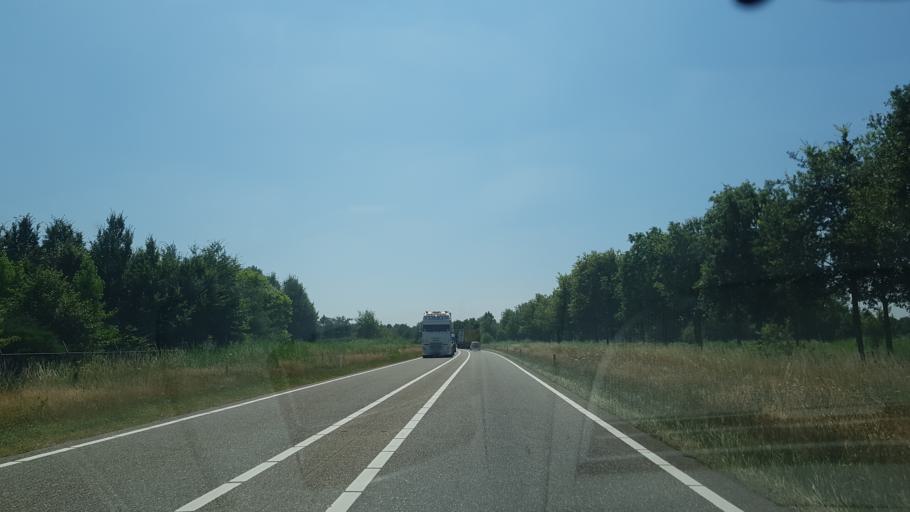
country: NL
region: North Brabant
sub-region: Gemeente Laarbeek
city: Aarle-Rixtel
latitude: 51.5225
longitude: 5.6565
